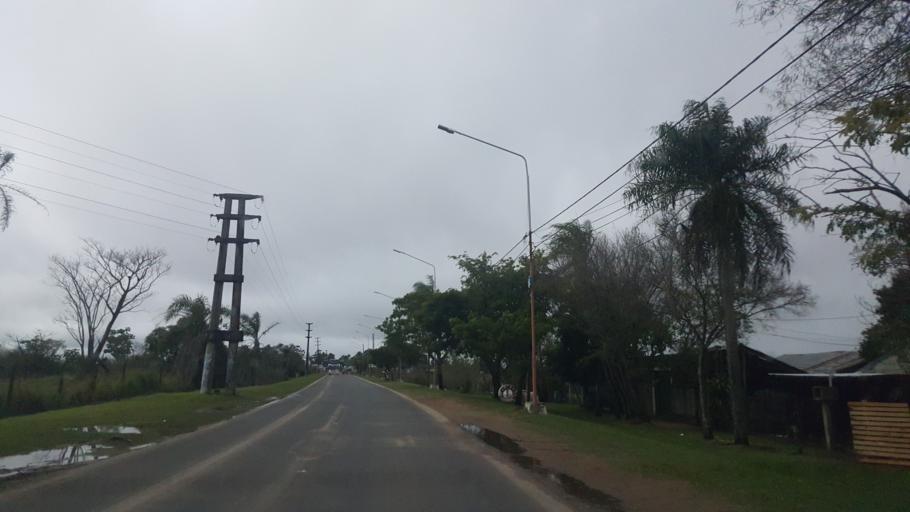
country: AR
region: Corrientes
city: Ituzaingo
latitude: -27.5936
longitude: -56.6838
